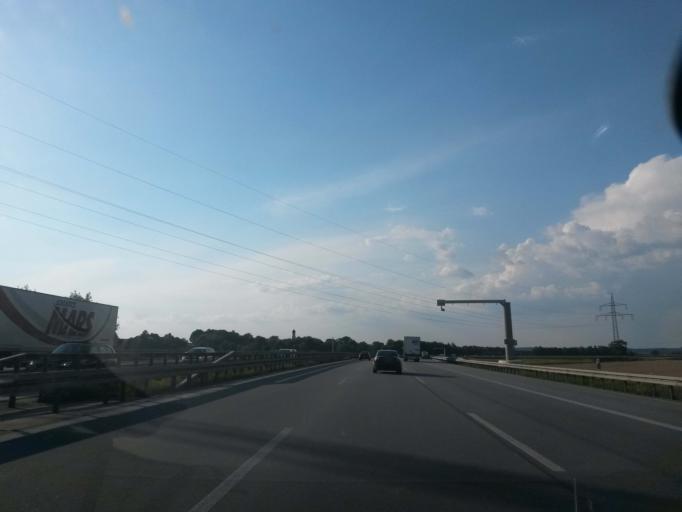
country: DE
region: Bavaria
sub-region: Upper Bavaria
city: Kranzberg
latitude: 48.3971
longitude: 11.5925
